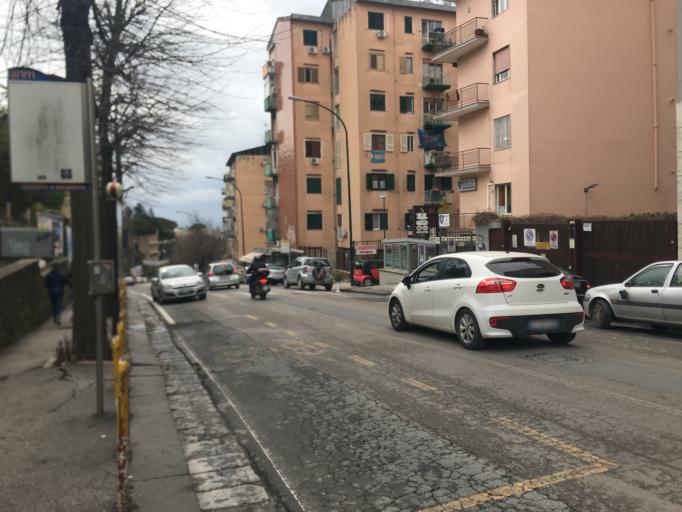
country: IT
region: Campania
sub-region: Provincia di Napoli
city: Napoli
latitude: 40.8612
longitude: 14.2246
